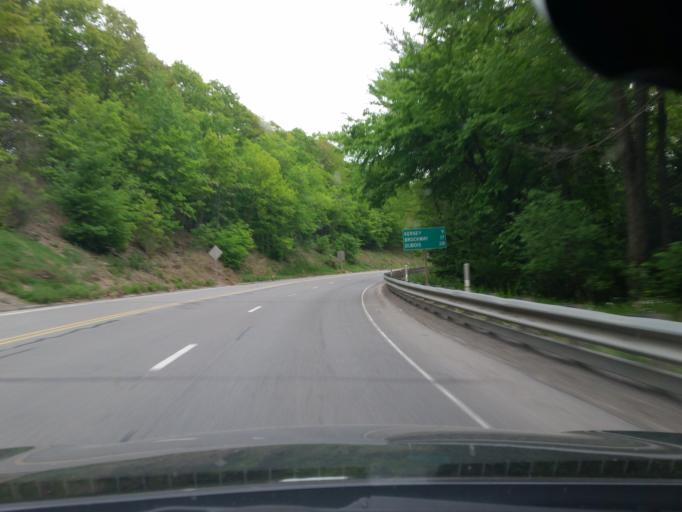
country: US
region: Pennsylvania
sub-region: Elk County
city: Ridgway
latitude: 41.4208
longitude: -78.7183
